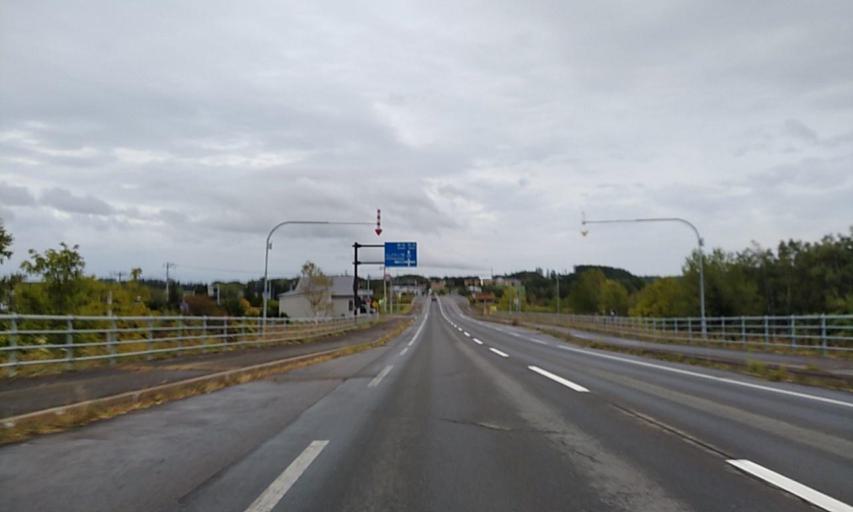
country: JP
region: Hokkaido
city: Kitami
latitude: 44.0792
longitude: 143.9335
